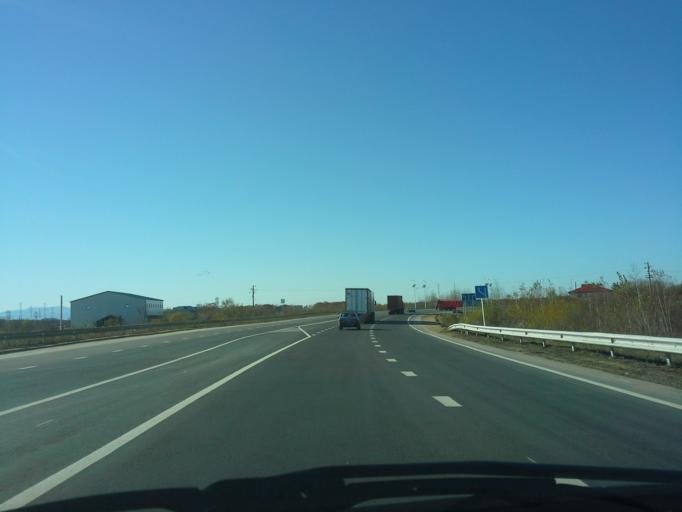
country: RU
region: Jewish Autonomous Oblast
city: Priamurskiy
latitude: 48.5190
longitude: 134.9128
